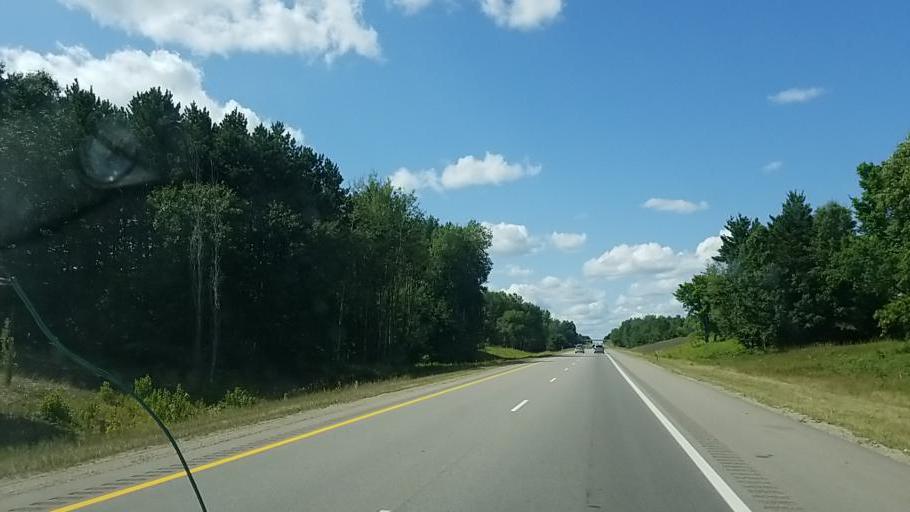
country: US
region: Michigan
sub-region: Mecosta County
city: Big Rapids
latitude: 43.6298
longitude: -85.5031
